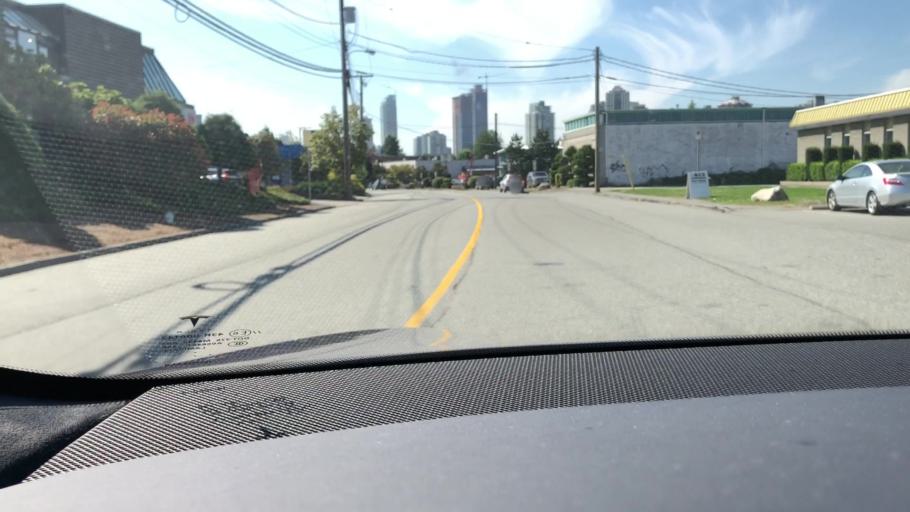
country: CA
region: British Columbia
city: Burnaby
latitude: 49.2587
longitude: -122.9792
